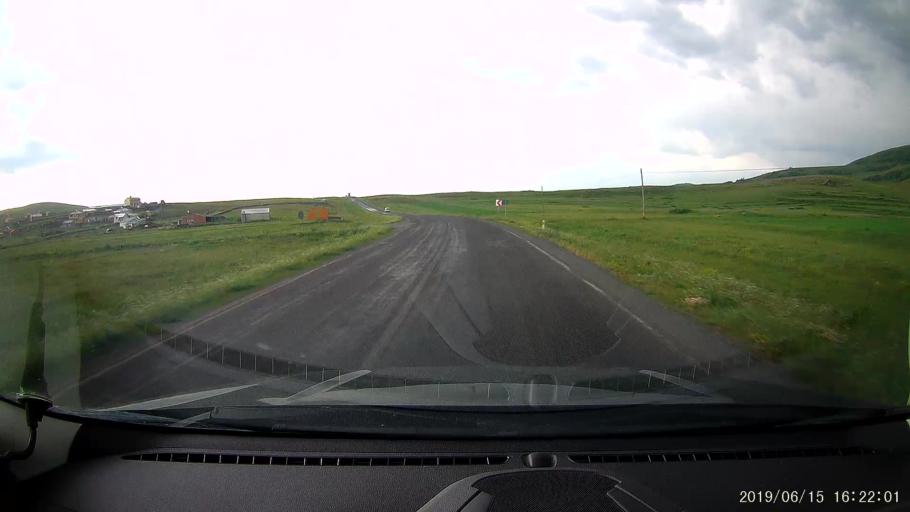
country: TR
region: Ardahan
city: Hanak
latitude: 41.1923
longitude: 42.8460
